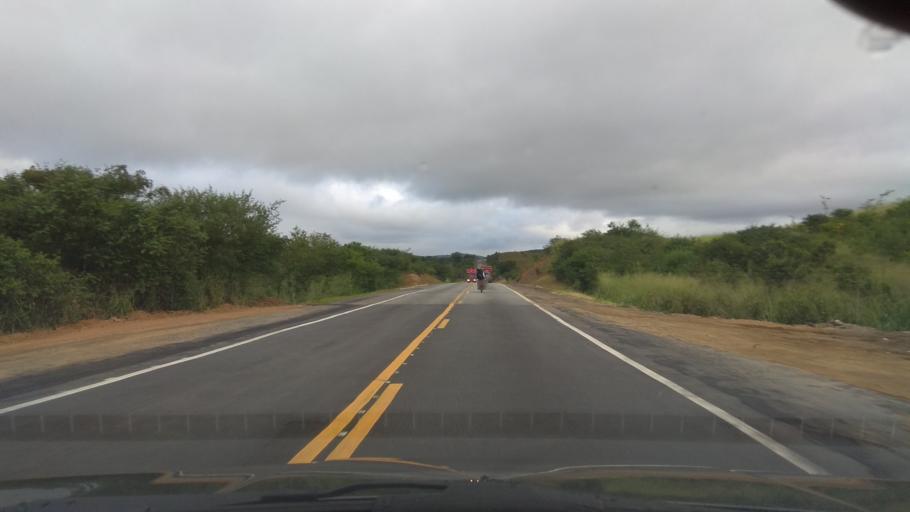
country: BR
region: Bahia
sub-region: Santa Ines
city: Santa Ines
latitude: -13.3163
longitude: -40.0171
